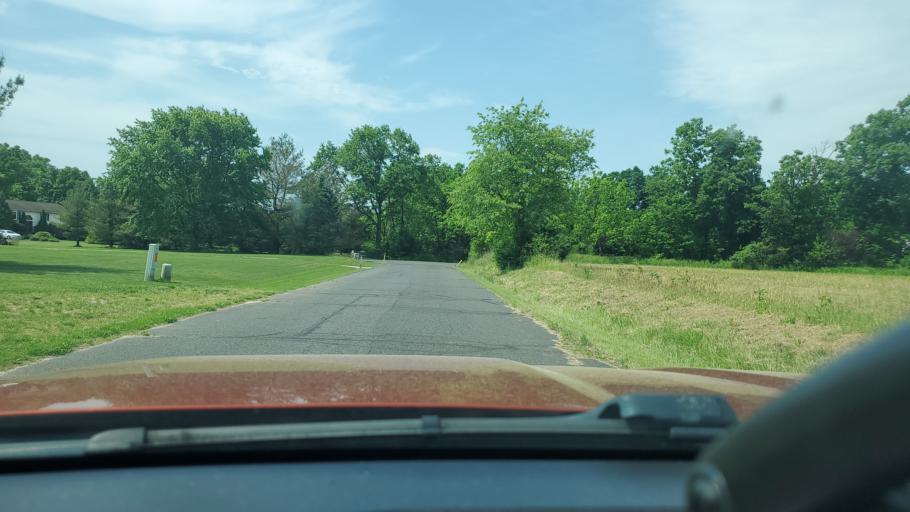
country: US
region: Pennsylvania
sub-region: Montgomery County
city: Limerick
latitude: 40.2861
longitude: -75.5122
